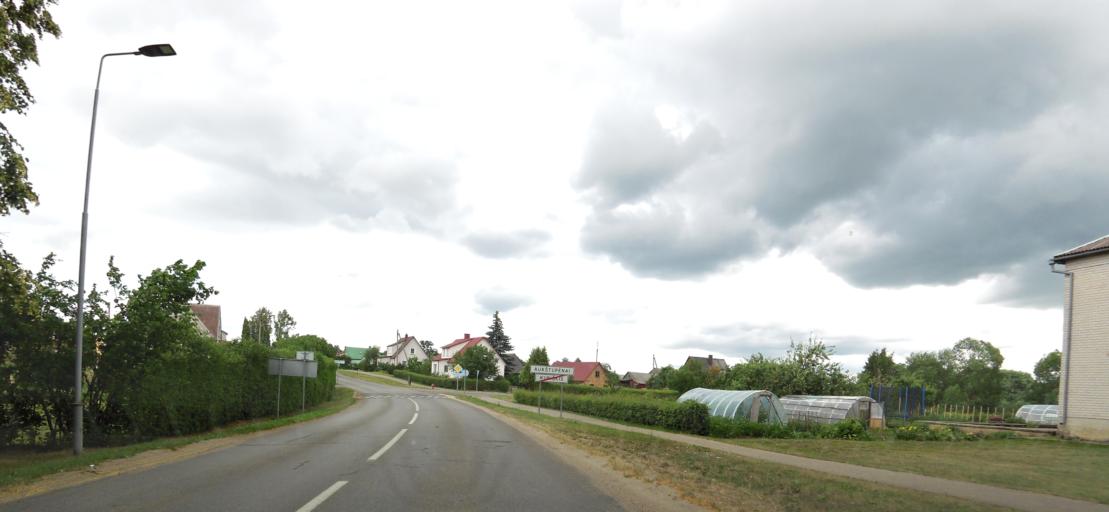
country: LT
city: Kupiskis
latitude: 55.8456
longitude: 24.9815
